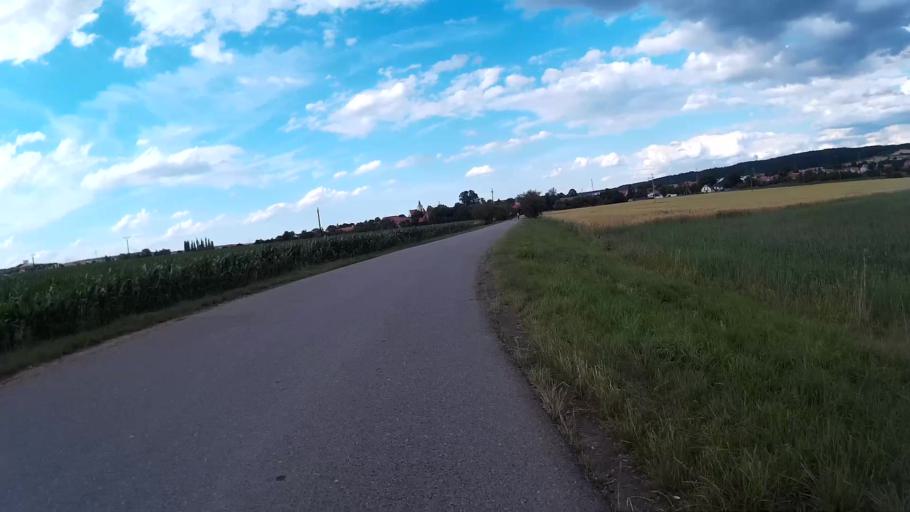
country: CZ
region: South Moravian
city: Ricany
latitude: 49.2063
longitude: 16.4047
